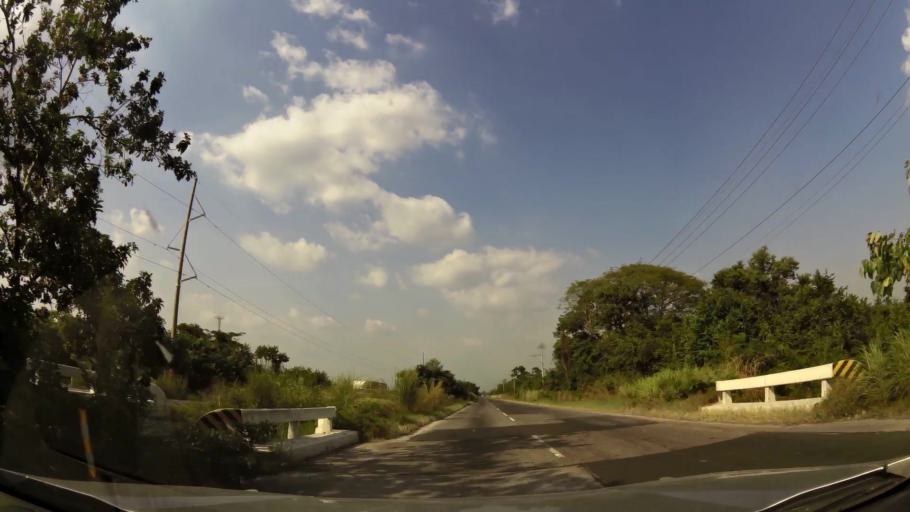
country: GT
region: Escuintla
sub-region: Municipio de Masagua
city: Masagua
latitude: 14.1140
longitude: -90.7813
